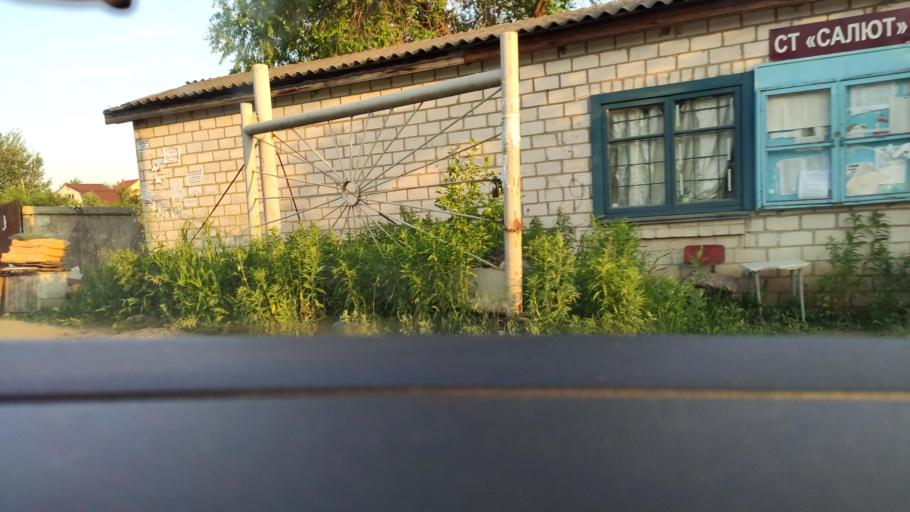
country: RU
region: Voronezj
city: Ramon'
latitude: 51.9069
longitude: 39.1772
